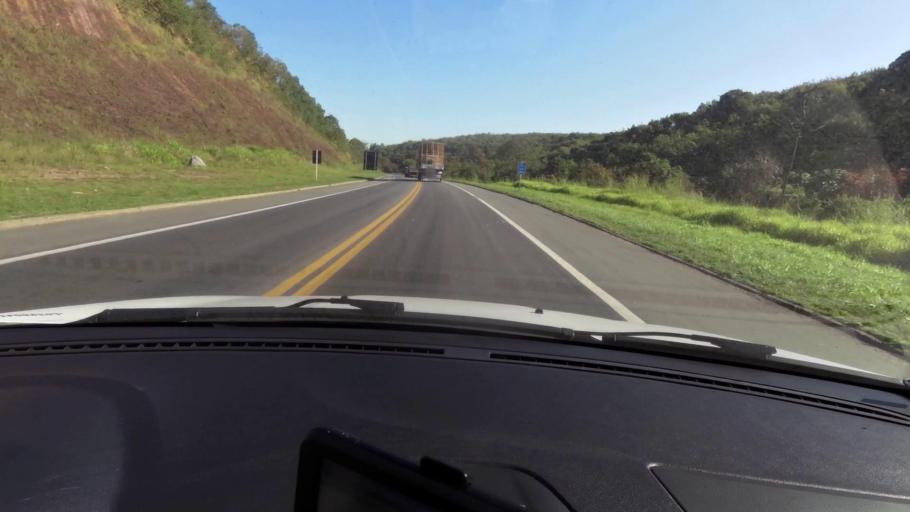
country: BR
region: Espirito Santo
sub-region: Alfredo Chaves
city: Alfredo Chaves
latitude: -20.6776
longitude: -40.6663
